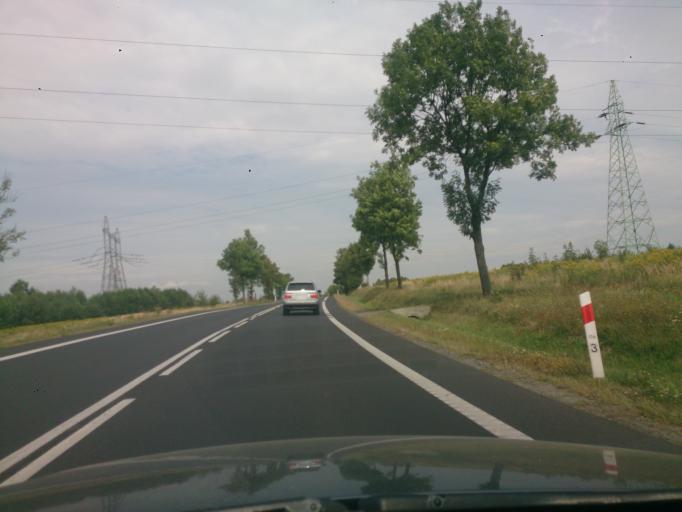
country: PL
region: Subcarpathian Voivodeship
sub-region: Powiat rzeszowski
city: Glogow Malopolski
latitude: 50.1945
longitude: 21.8857
